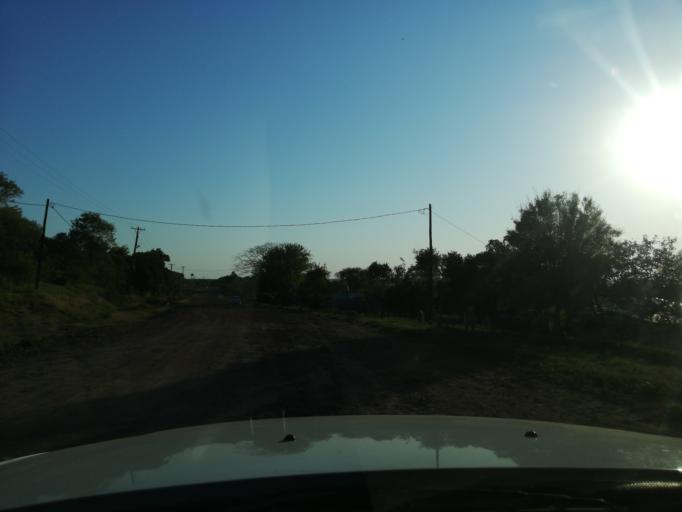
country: AR
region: Misiones
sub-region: Departamento de Apostoles
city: San Jose
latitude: -27.6308
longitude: -55.7268
